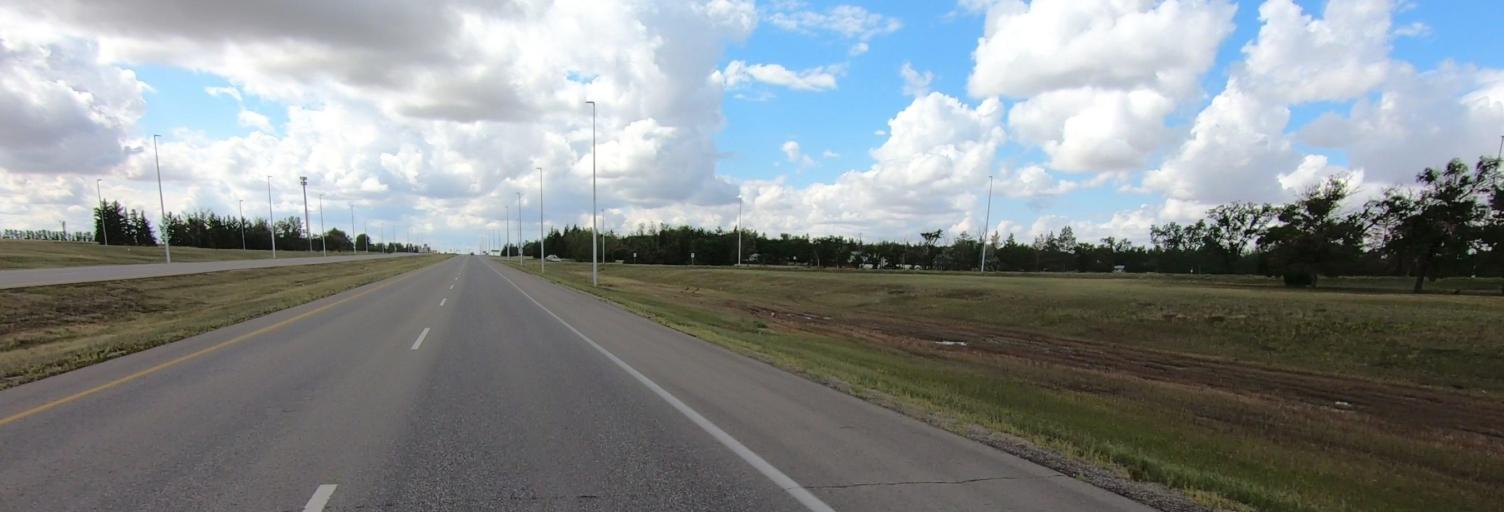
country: CA
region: Saskatchewan
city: Regina
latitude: 50.4072
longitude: -104.5904
